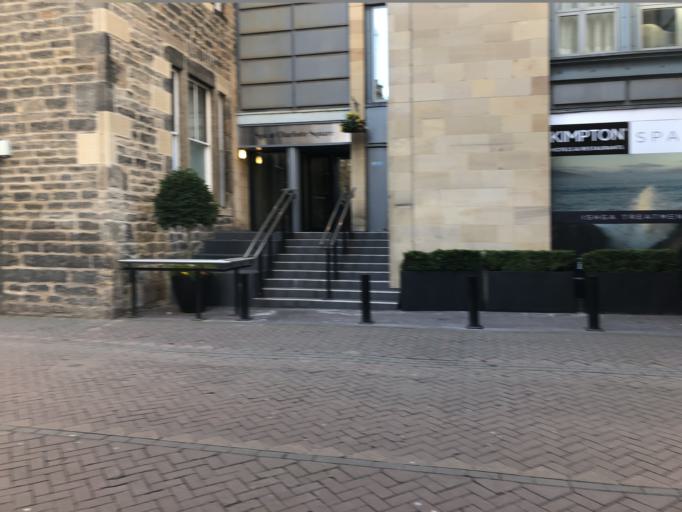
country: GB
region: Scotland
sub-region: Edinburgh
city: Edinburgh
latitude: 55.9512
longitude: -3.2056
